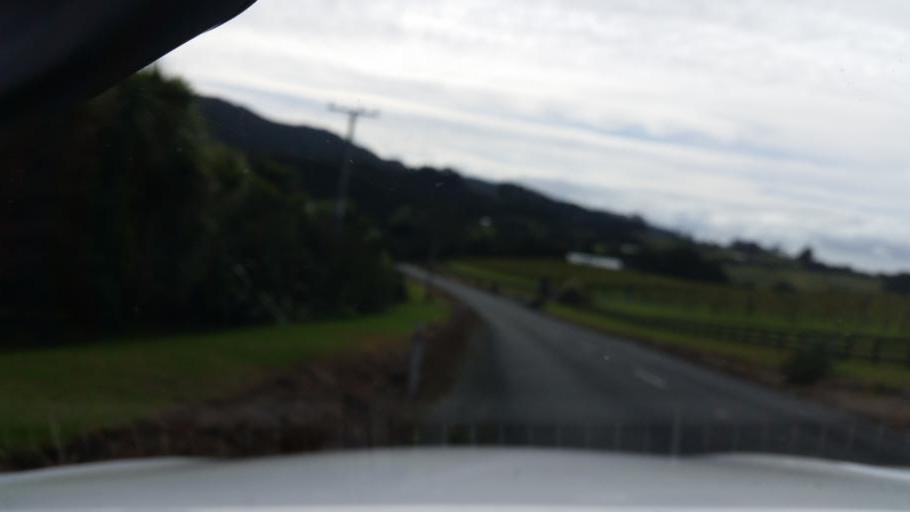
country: NZ
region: Auckland
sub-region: Auckland
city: Wellsford
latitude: -36.0897
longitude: 174.5331
